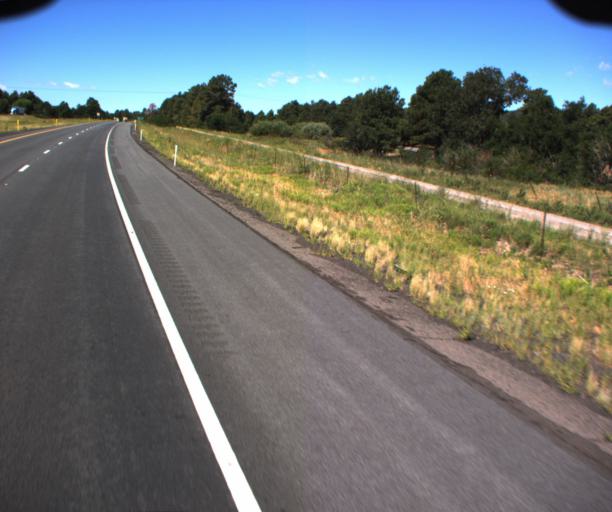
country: US
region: Arizona
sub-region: Coconino County
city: Williams
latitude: 35.2379
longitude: -112.2220
